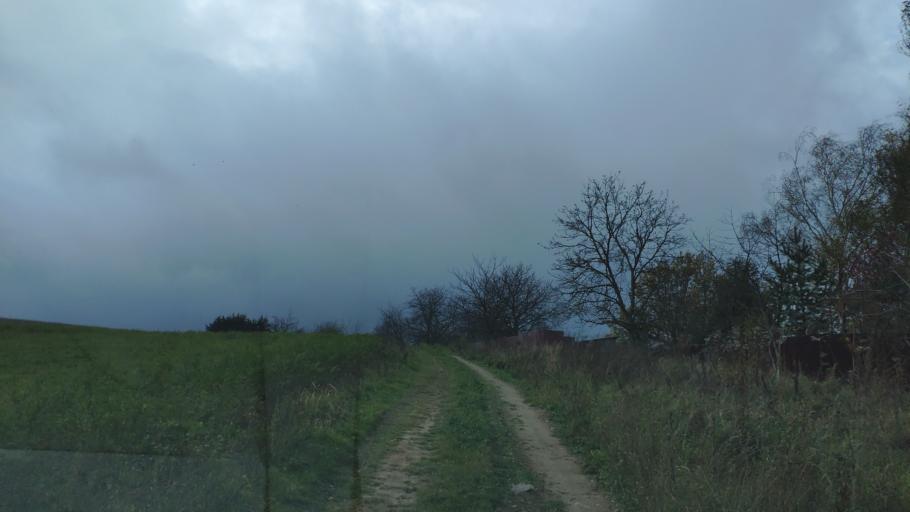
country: SK
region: Presovsky
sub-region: Okres Presov
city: Presov
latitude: 49.0102
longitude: 21.1904
